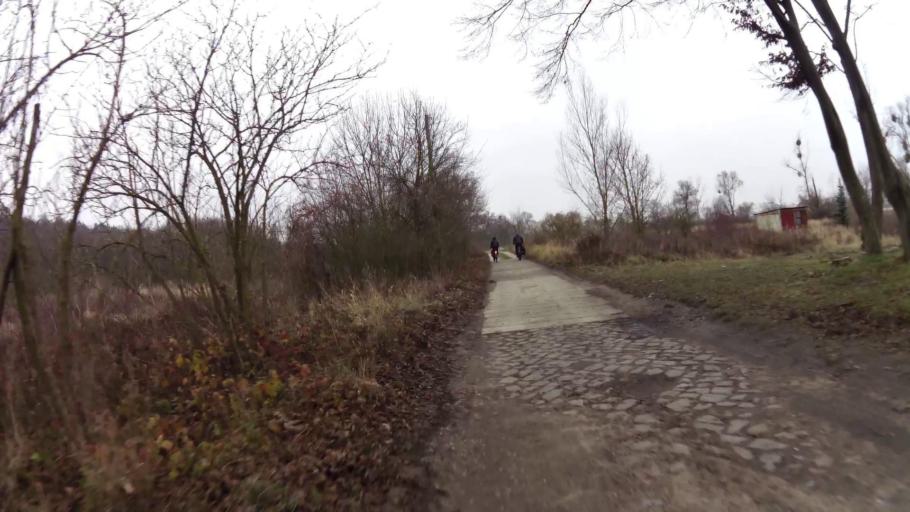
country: DE
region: Brandenburg
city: Schoneberg
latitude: 52.9344
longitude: 14.1462
